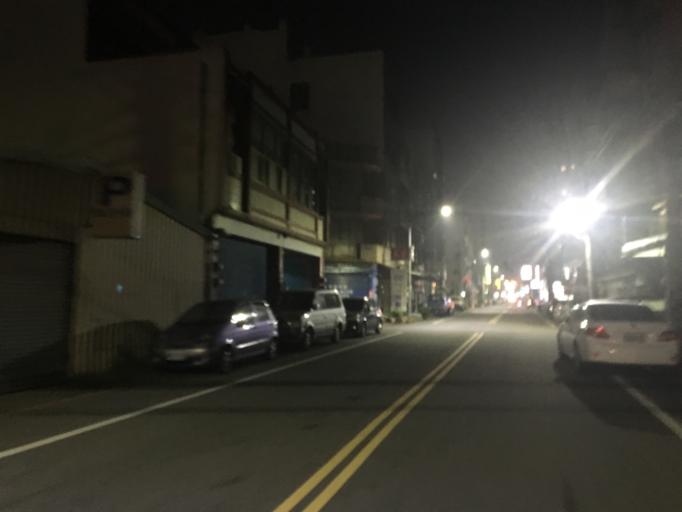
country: TW
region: Taiwan
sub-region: Hsinchu
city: Hsinchu
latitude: 24.8218
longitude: 120.9776
